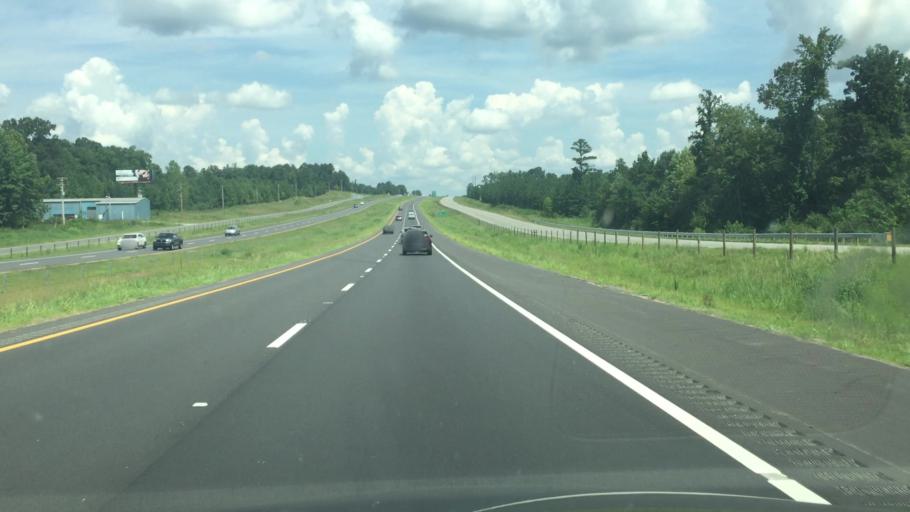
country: US
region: North Carolina
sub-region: Richmond County
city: Ellerbe
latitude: 35.0256
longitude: -79.7696
